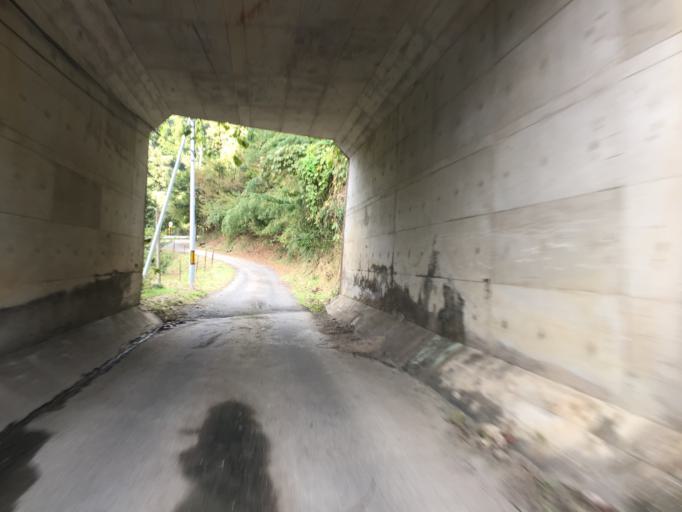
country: JP
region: Miyagi
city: Marumori
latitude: 37.9337
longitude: 140.7062
